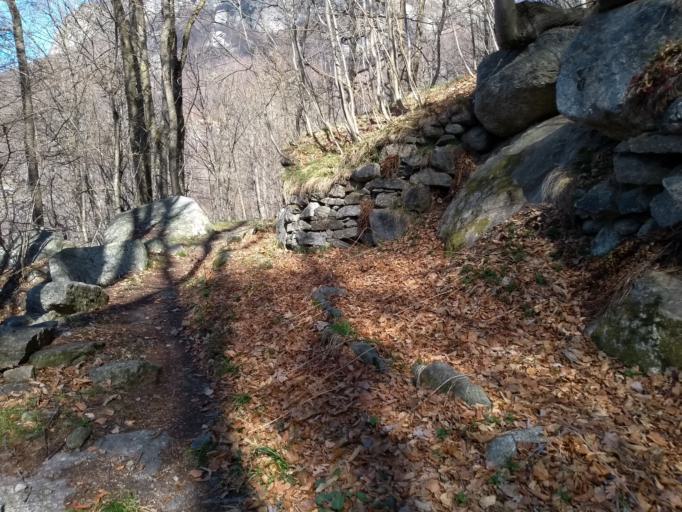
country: IT
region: Piedmont
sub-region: Provincia di Torino
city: Chialamberto
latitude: 45.3696
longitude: 7.3473
